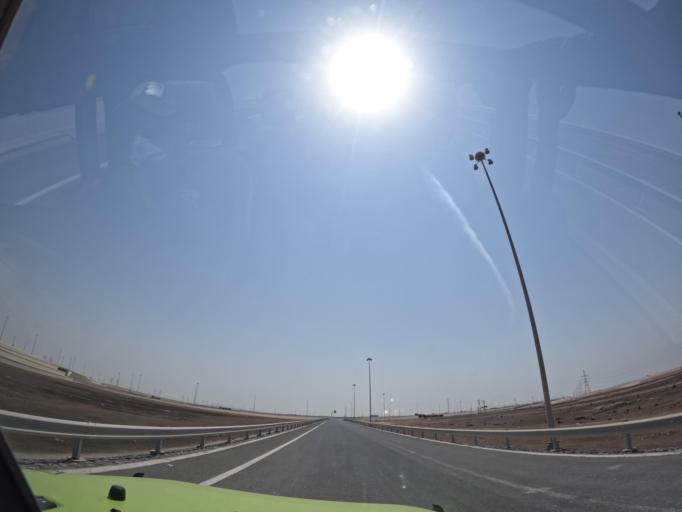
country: AE
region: Abu Dhabi
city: Abu Dhabi
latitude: 24.2156
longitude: 54.4121
